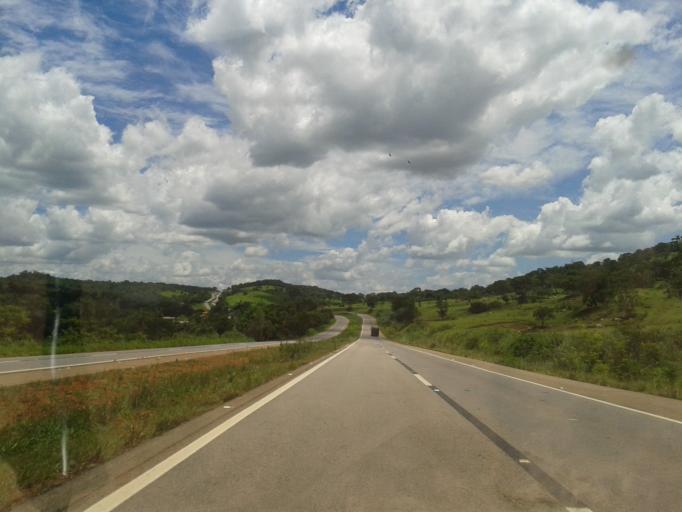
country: BR
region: Goias
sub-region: Neropolis
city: Neropolis
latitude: -16.3431
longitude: -49.2614
